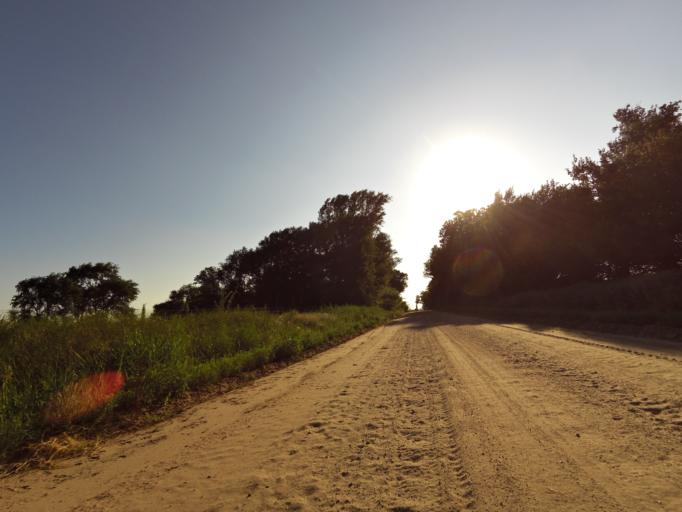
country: US
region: Kansas
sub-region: McPherson County
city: Inman
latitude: 38.1883
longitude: -97.8795
